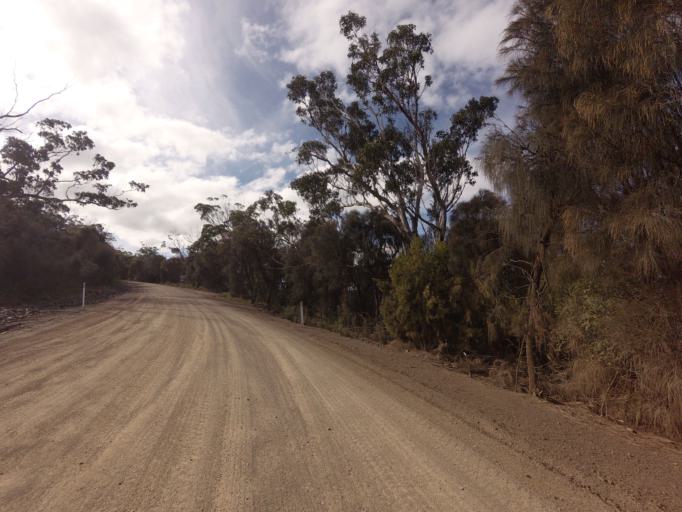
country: AU
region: Tasmania
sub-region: Clarence
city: Sandford
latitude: -43.0966
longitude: 147.7210
